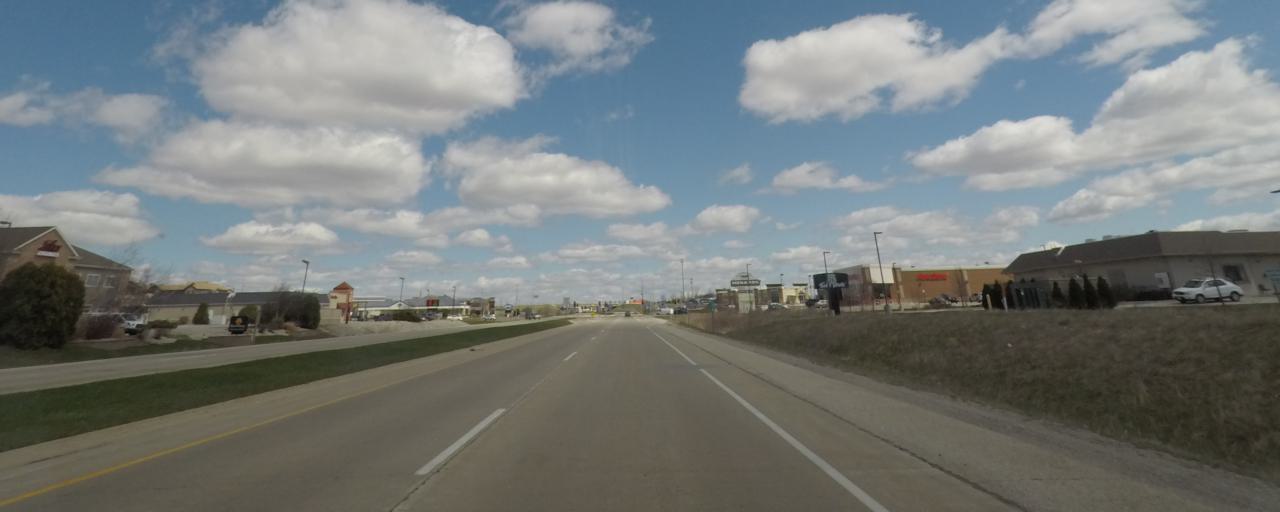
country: US
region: Wisconsin
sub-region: Jefferson County
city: Johnson Creek
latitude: 43.0808
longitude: -88.7643
